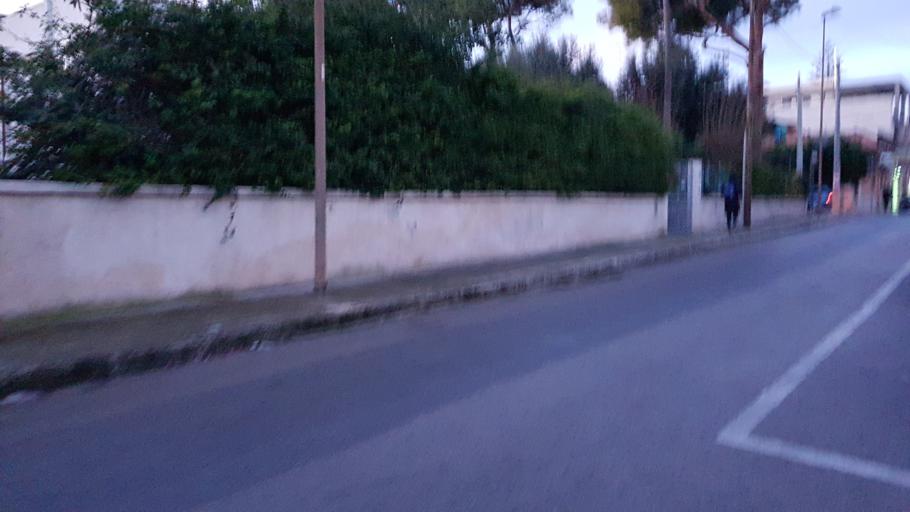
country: IT
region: Apulia
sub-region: Provincia di Brindisi
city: Brindisi
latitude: 40.6463
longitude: 17.9428
